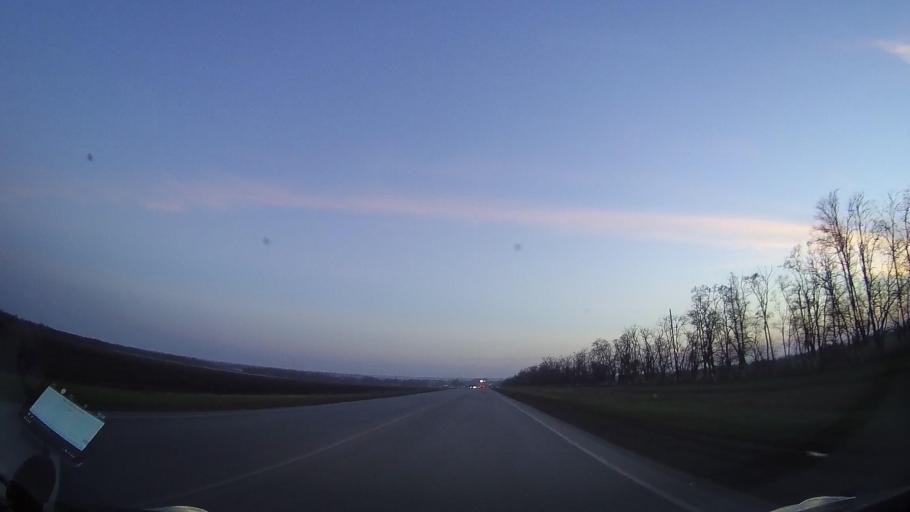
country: RU
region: Rostov
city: Zernograd
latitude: 46.8182
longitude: 40.2994
